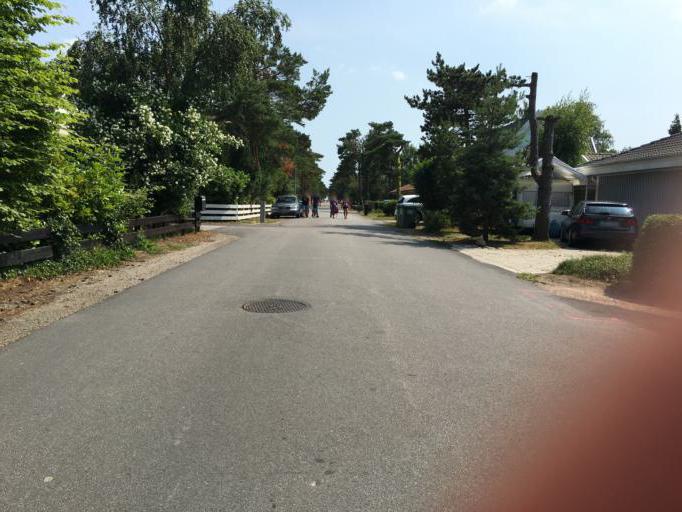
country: SE
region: Skane
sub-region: Vellinge Kommun
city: Hollviken
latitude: 55.4059
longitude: 12.9467
